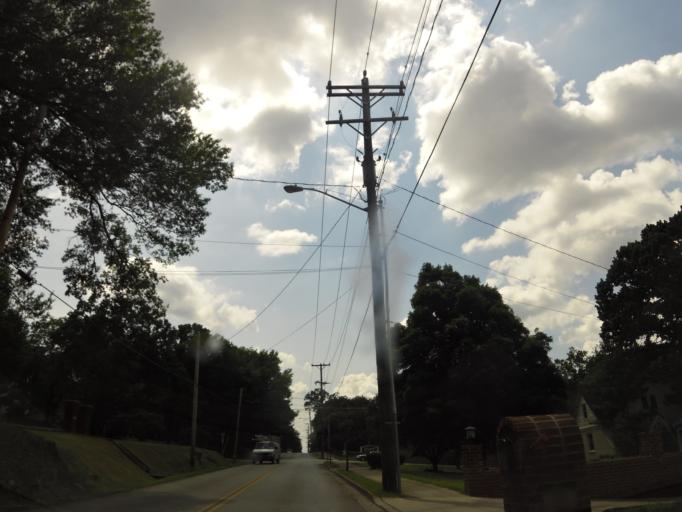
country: US
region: Tennessee
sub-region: Davidson County
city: Oak Hill
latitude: 36.1210
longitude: -86.7786
